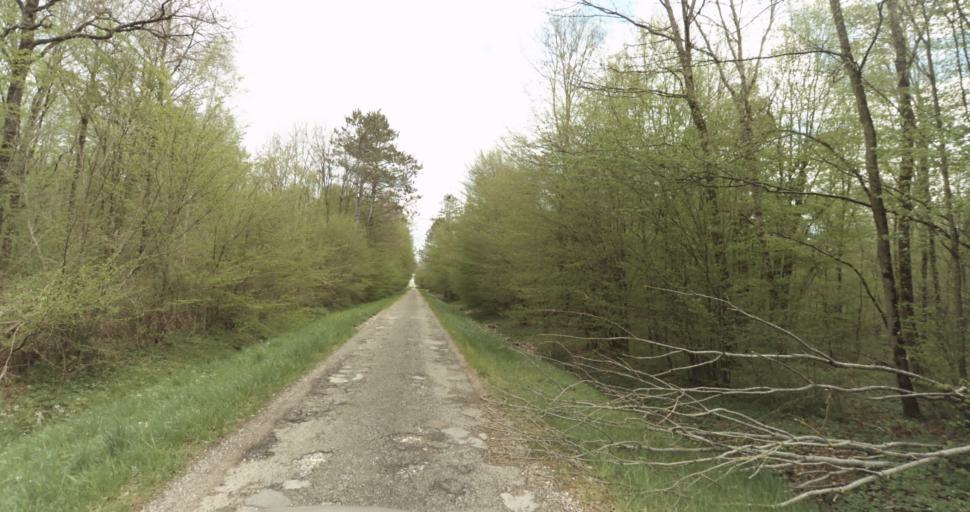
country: FR
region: Franche-Comte
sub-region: Departement du Jura
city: Champvans
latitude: 47.1519
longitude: 5.4207
